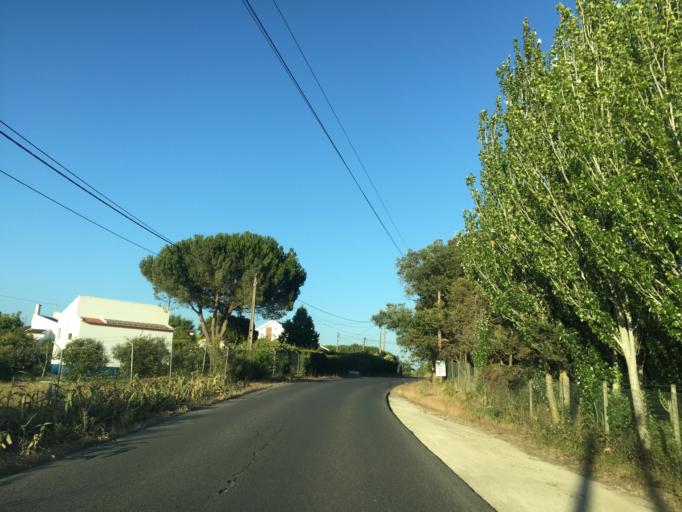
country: PT
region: Santarem
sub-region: Cartaxo
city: Cartaxo
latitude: 39.1670
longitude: -8.8057
